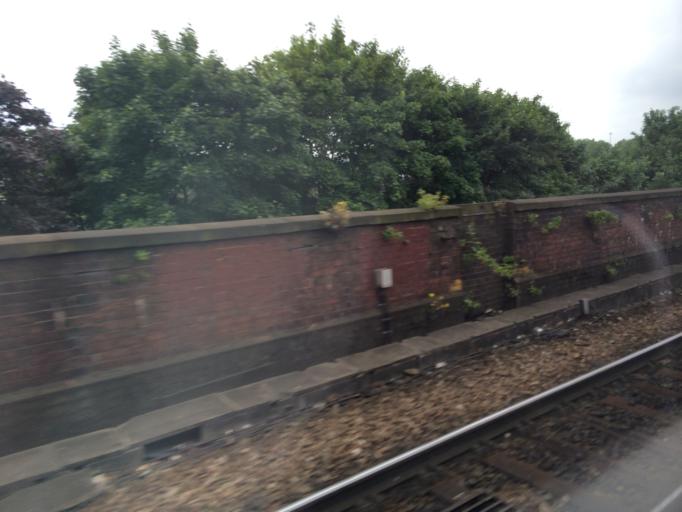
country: GB
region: England
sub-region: Manchester
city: Manchester
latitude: 53.4730
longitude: -2.2178
